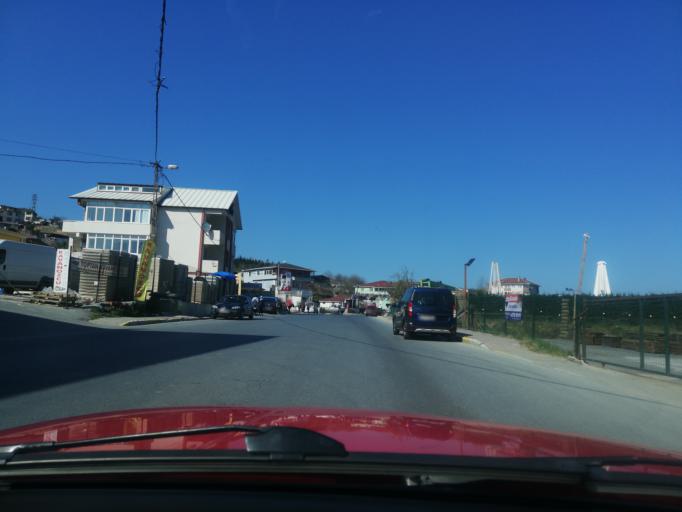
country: TR
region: Istanbul
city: Umraniye
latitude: 41.0916
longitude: 29.1418
